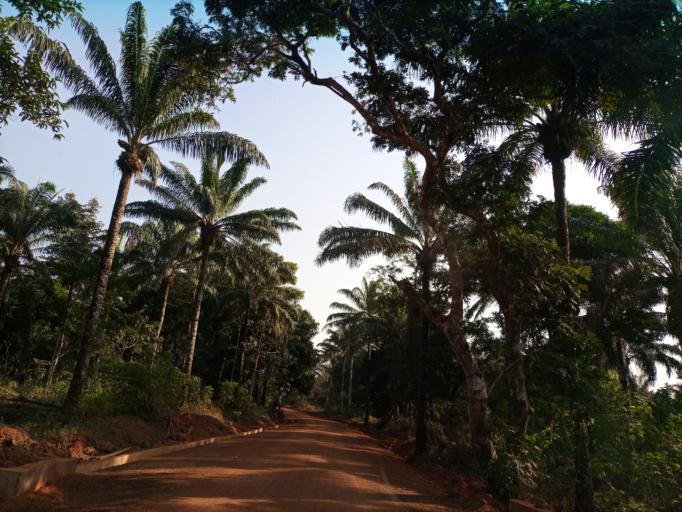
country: NG
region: Enugu
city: Opi
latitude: 6.7742
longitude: 7.3904
